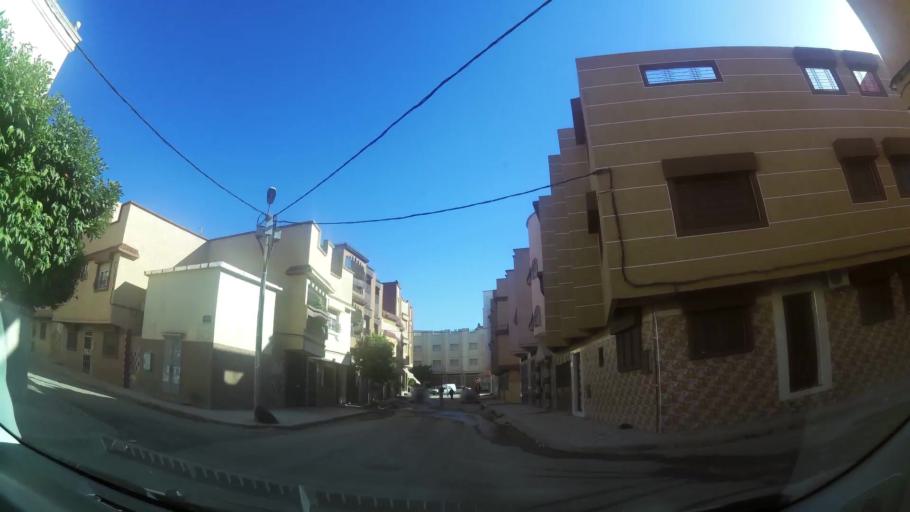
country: MA
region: Oriental
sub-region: Berkane-Taourirt
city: Ahfir
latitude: 34.9569
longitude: -2.1036
